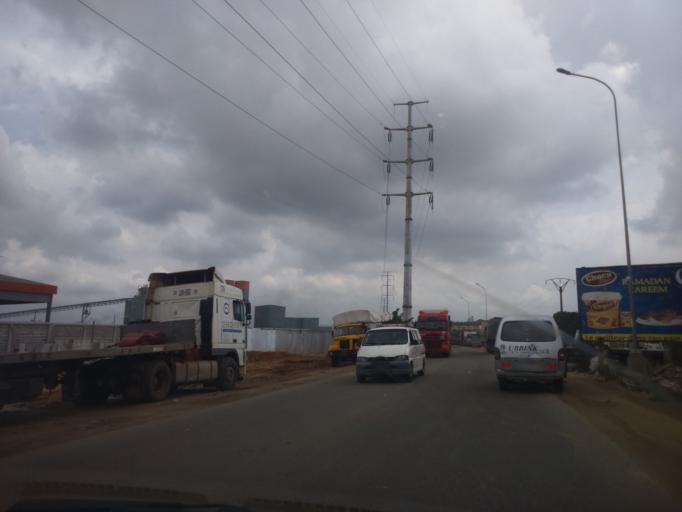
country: CI
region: Lagunes
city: Abobo
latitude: 5.3837
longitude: -4.0758
